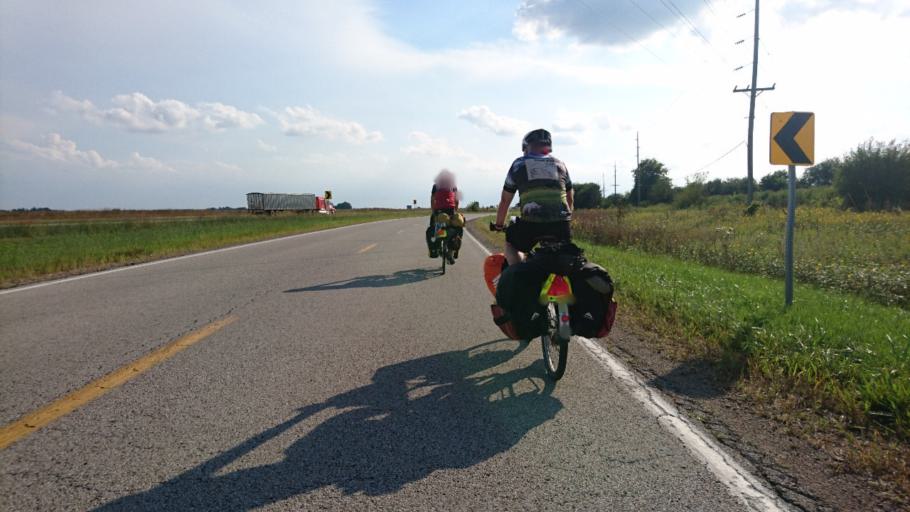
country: US
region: Illinois
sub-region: Logan County
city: Atlanta
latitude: 40.3032
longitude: -89.1825
